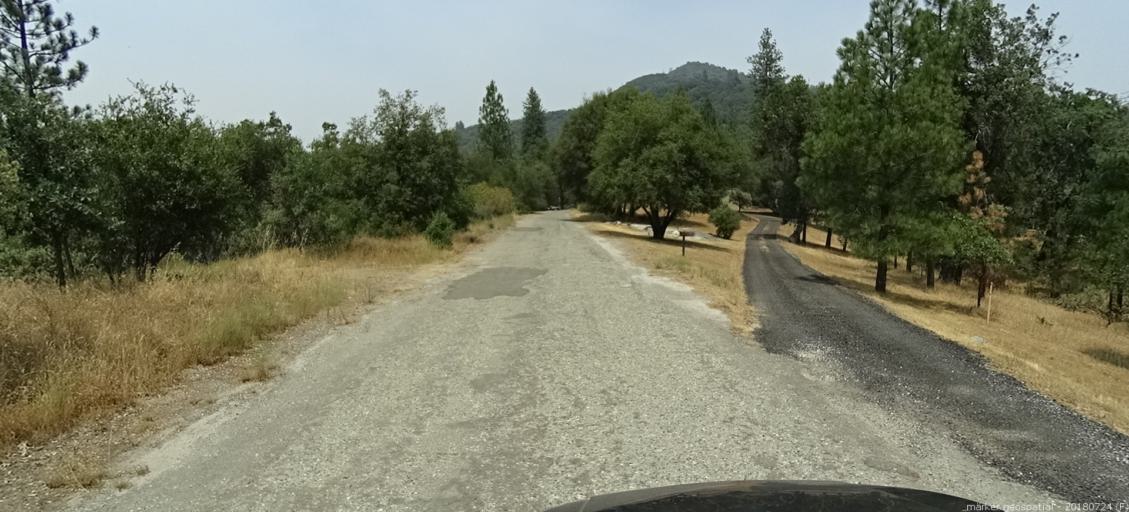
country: US
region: California
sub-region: Madera County
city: Oakhurst
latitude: 37.2528
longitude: -119.5567
